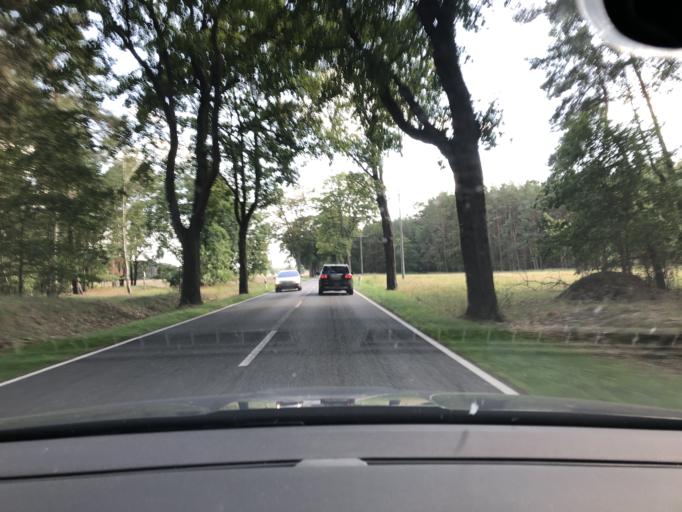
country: DE
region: Brandenburg
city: Ruthnick
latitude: 52.8920
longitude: 12.9856
